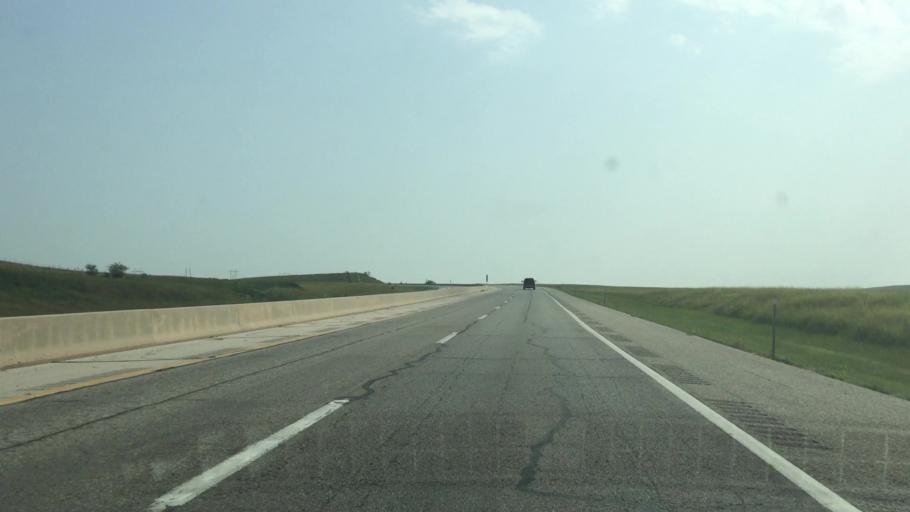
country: US
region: Kansas
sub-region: Chase County
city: Cottonwood Falls
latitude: 38.1761
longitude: -96.4677
